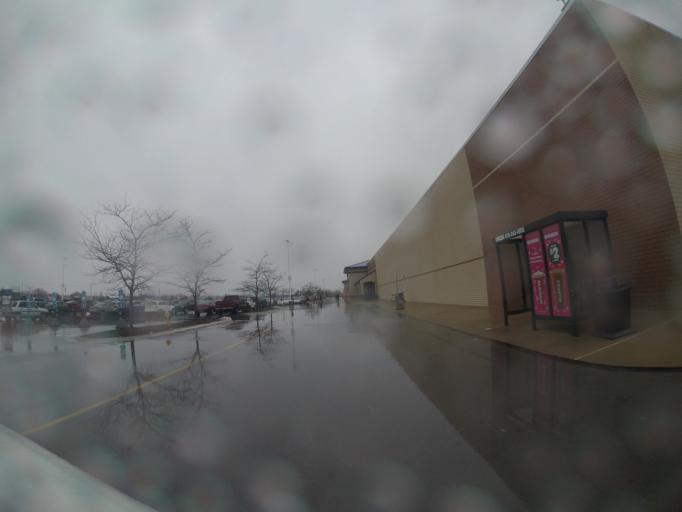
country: US
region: Ohio
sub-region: Wood County
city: Perrysburg
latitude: 41.5465
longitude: -83.5878
